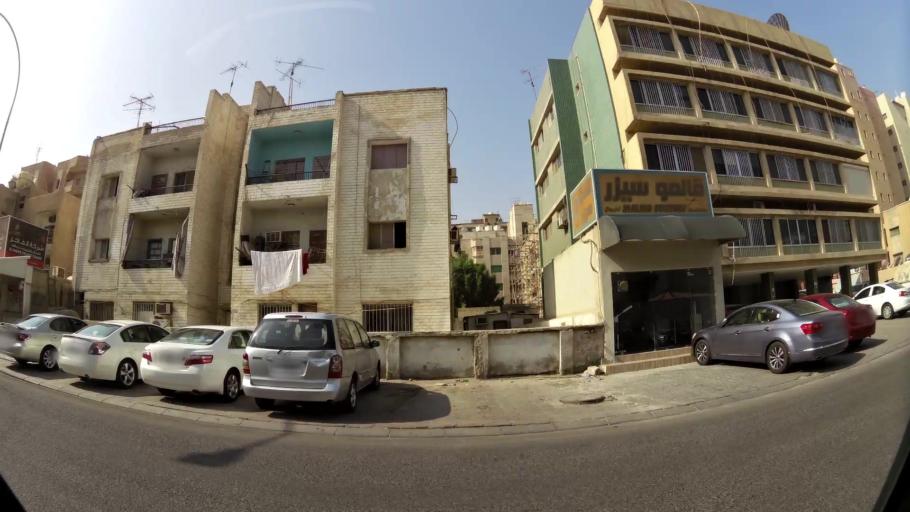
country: KW
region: Muhafazat Hawalli
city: Hawalli
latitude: 29.3382
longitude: 48.0112
